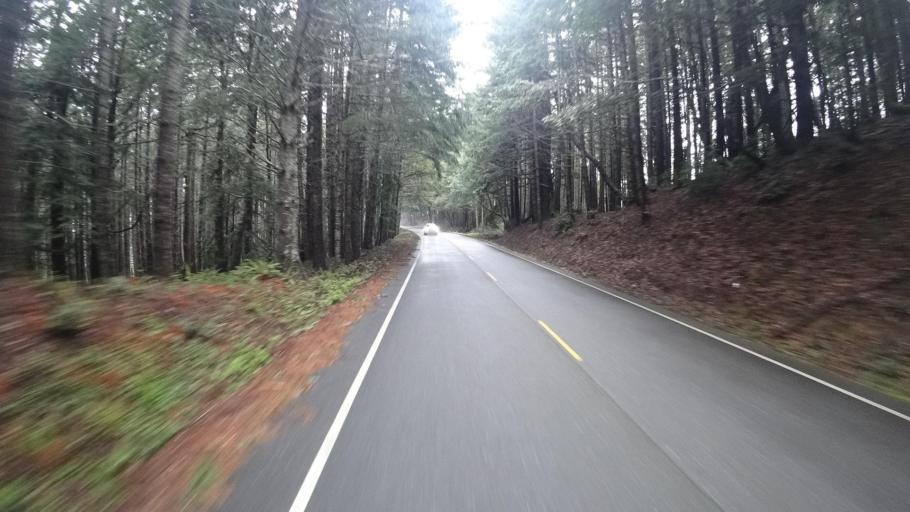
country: US
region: California
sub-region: Humboldt County
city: Westhaven-Moonstone
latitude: 41.2018
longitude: -123.9446
